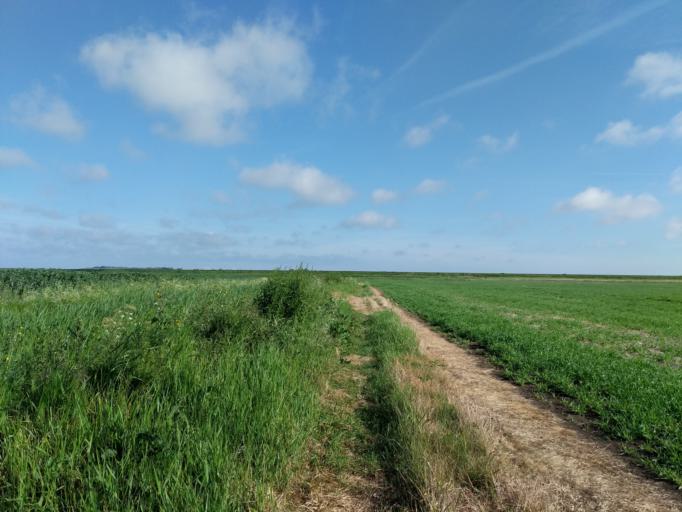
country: GB
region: England
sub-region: Kent
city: Faversham
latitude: 51.3400
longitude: 0.9197
